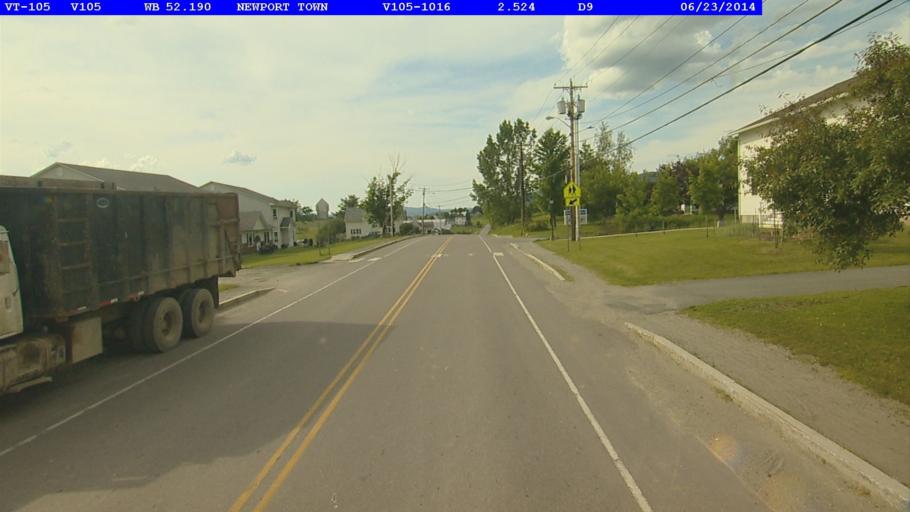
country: US
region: Vermont
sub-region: Orleans County
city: Newport
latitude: 44.9512
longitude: -72.3070
